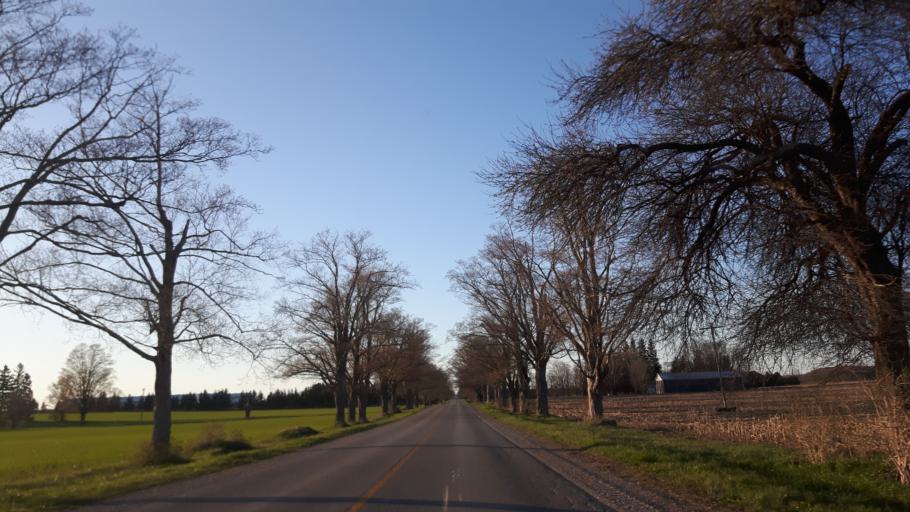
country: CA
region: Ontario
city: Bluewater
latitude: 43.5302
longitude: -81.5440
